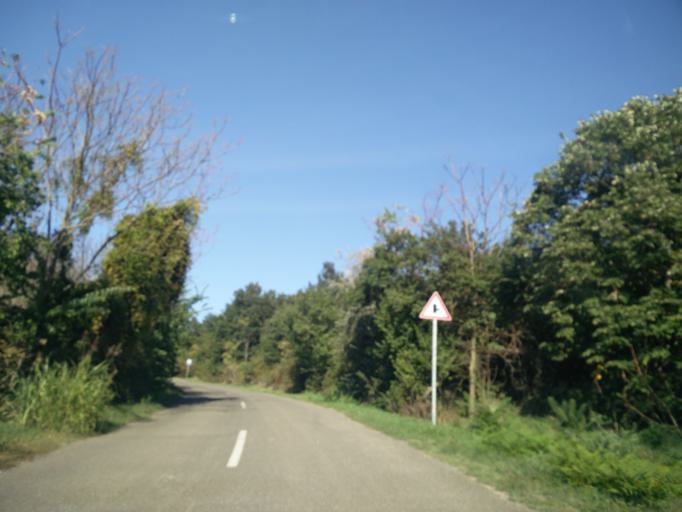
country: HU
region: Fejer
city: Pakozd
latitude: 47.2183
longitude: 18.5779
